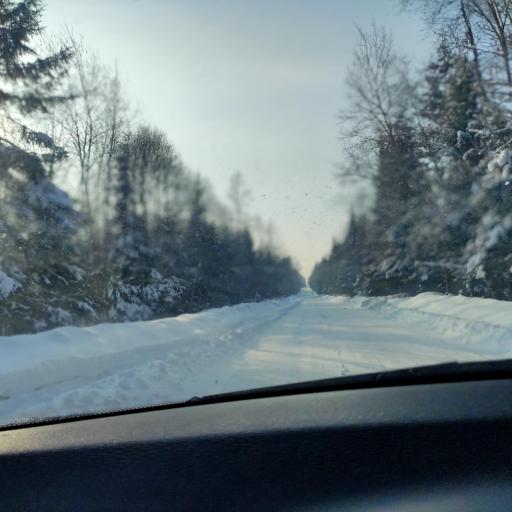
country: RU
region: Perm
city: Kondratovo
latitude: 58.0768
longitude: 56.1297
